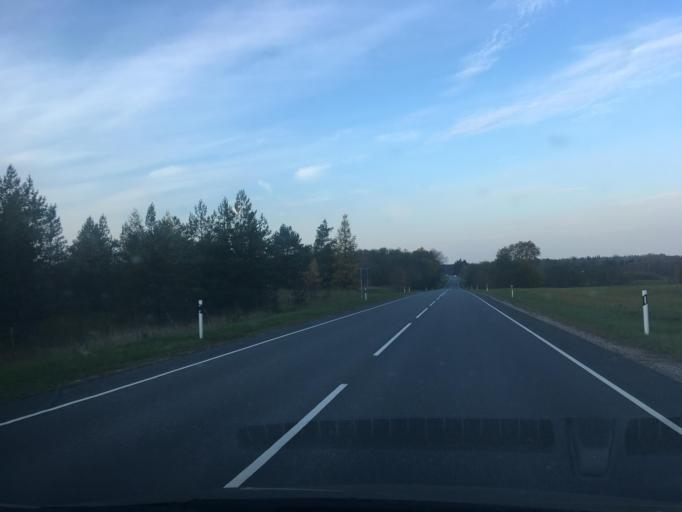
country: EE
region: Harju
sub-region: Nissi vald
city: Riisipere
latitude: 59.1199
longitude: 24.2909
